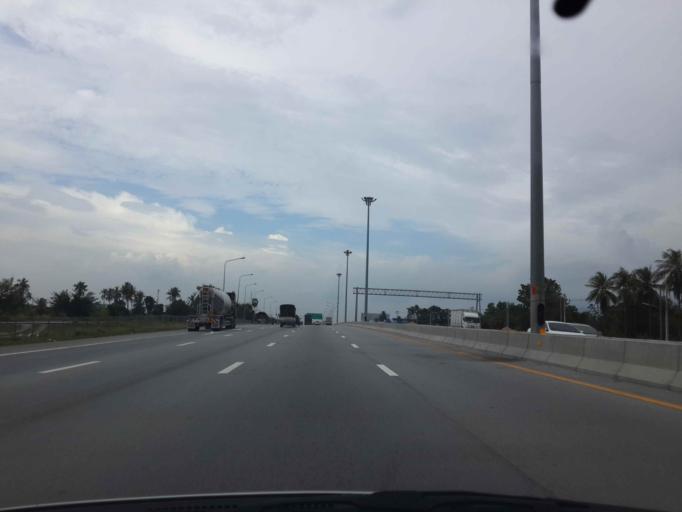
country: TH
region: Chon Buri
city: Chon Buri
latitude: 13.3161
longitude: 101.0084
